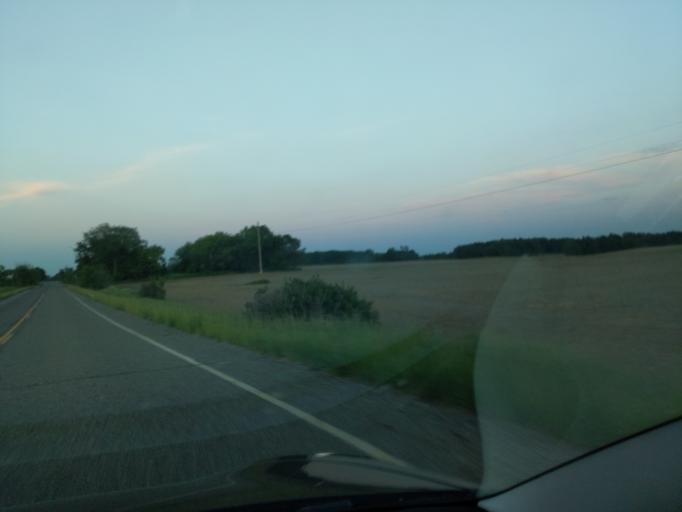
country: US
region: Michigan
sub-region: Barry County
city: Nashville
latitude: 42.5383
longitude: -85.0475
